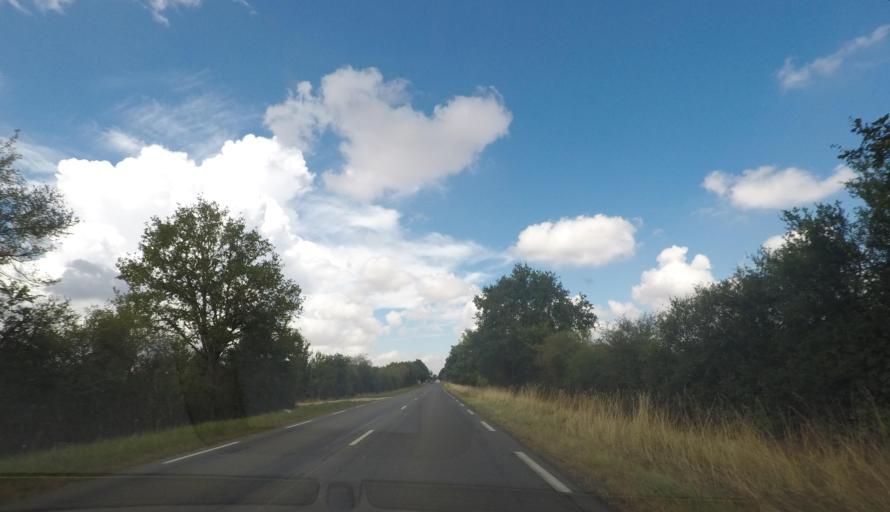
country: FR
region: Pays de la Loire
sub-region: Departement de la Sarthe
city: Bonnetable
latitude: 48.2170
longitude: 0.4317
